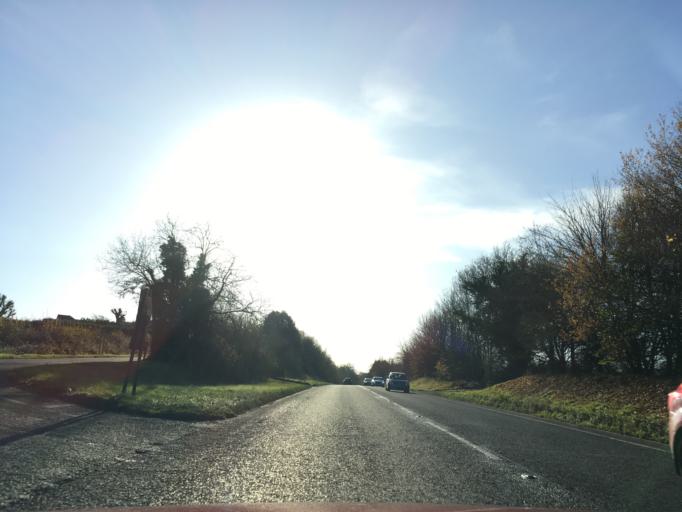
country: GB
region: England
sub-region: Wiltshire
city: Burbage
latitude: 51.3645
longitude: -1.6767
